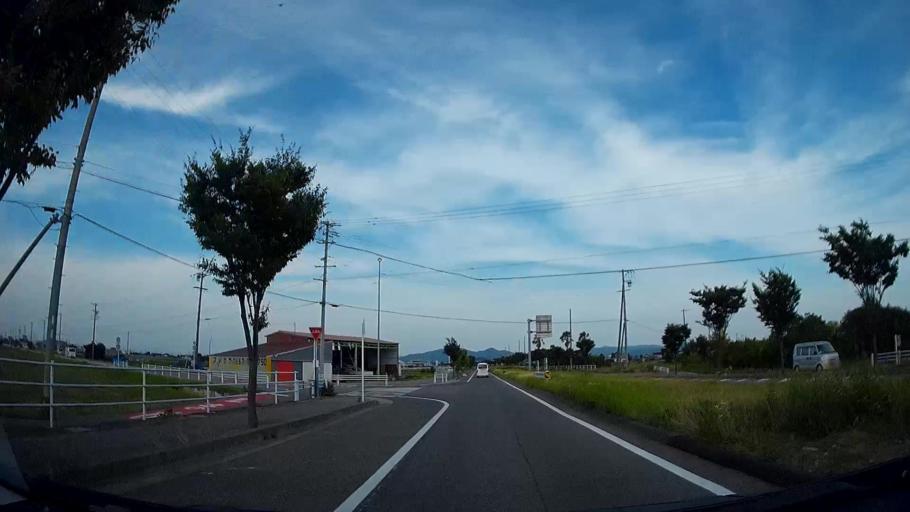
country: JP
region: Aichi
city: Nishio
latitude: 34.8477
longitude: 137.0389
